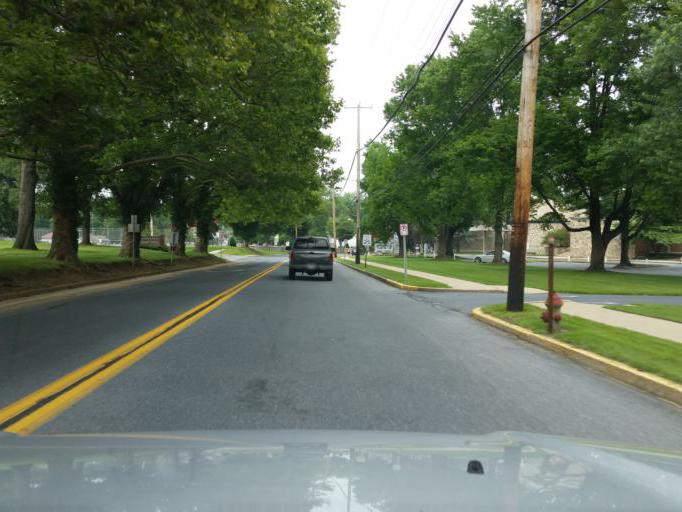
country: US
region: Pennsylvania
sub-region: Lancaster County
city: Lititz
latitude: 40.1547
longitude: -76.3130
